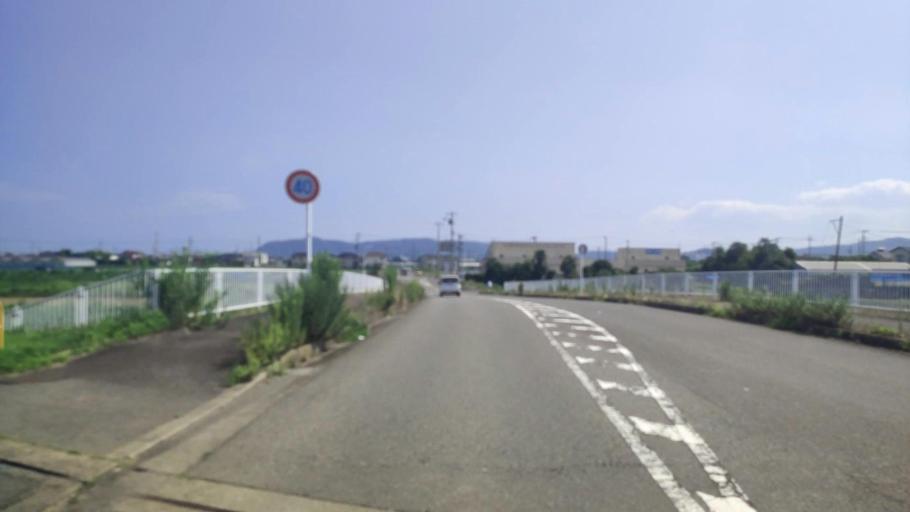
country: JP
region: Kanagawa
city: Isehara
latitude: 35.3666
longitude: 139.3169
